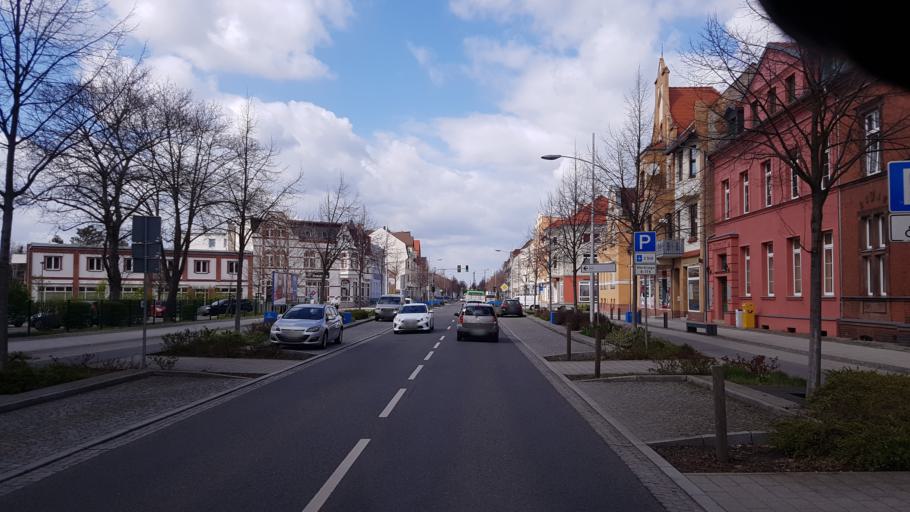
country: DE
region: Brandenburg
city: Senftenberg
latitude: 51.5213
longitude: 14.0049
